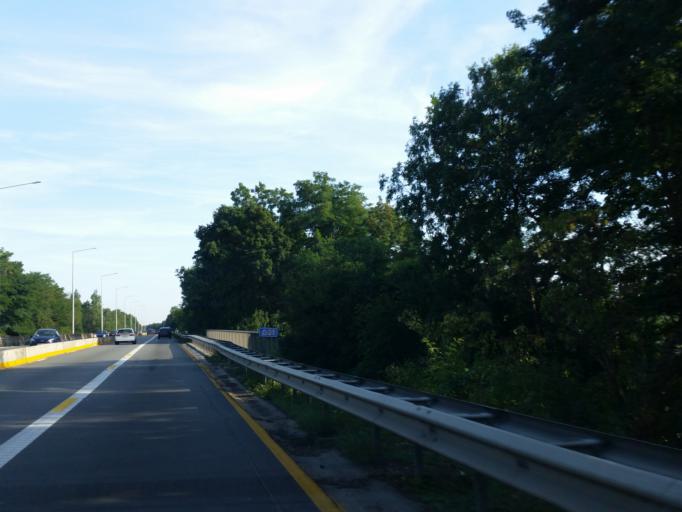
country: BE
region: Flanders
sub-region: Provincie Antwerpen
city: Mechelen
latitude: 51.0155
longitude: 4.4499
